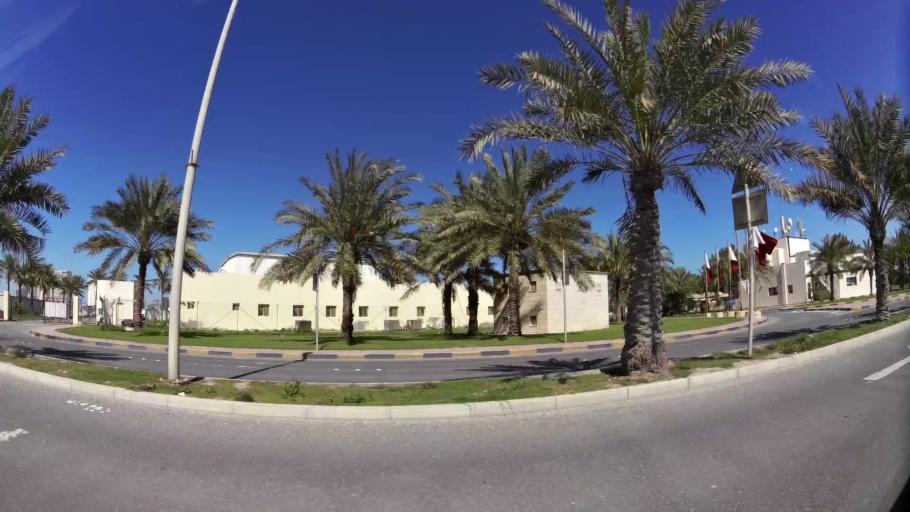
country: BH
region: Muharraq
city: Al Hadd
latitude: 26.2792
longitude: 50.6615
